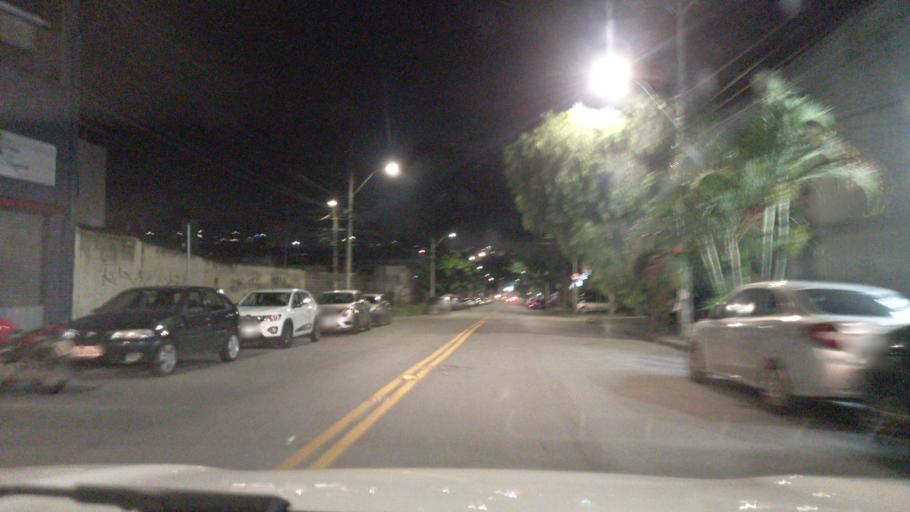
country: BR
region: Minas Gerais
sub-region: Belo Horizonte
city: Belo Horizonte
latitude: -19.8858
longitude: -43.9399
